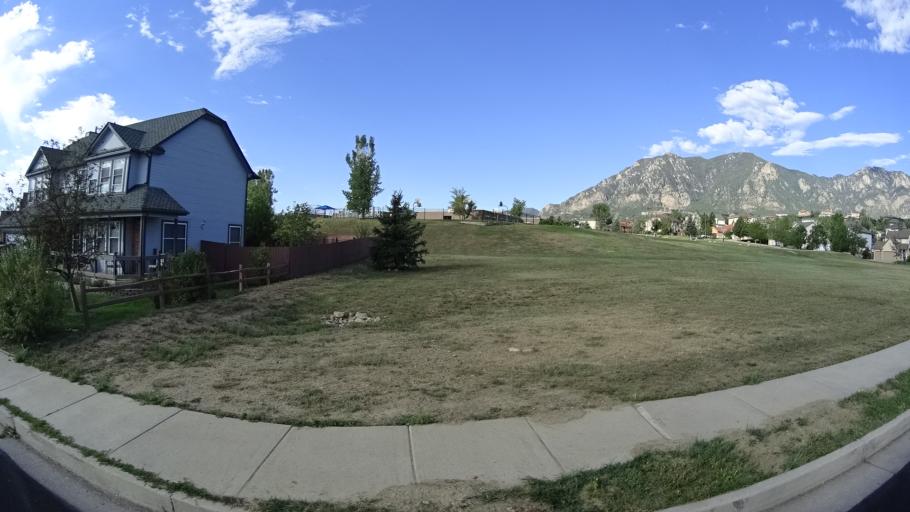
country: US
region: Colorado
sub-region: El Paso County
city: Fort Carson
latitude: 38.7583
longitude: -104.8133
